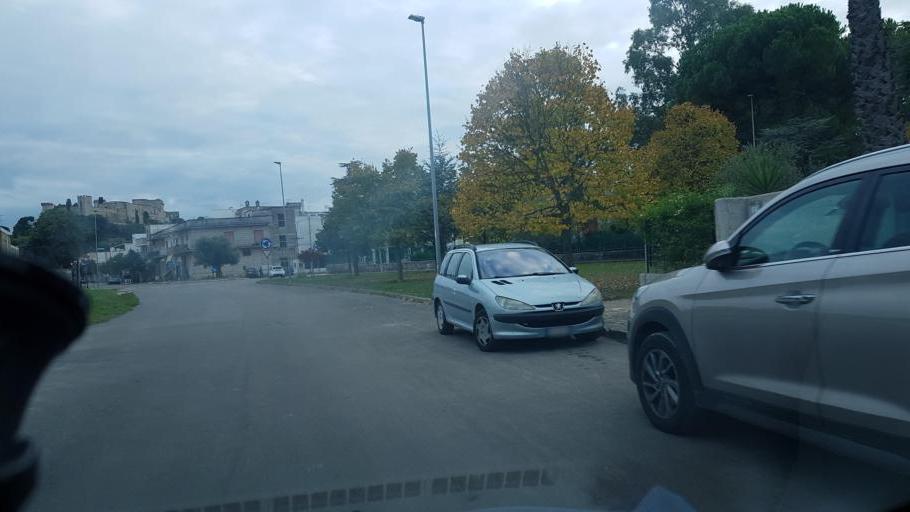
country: IT
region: Apulia
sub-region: Provincia di Brindisi
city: Oria
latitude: 40.5046
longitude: 17.6395
